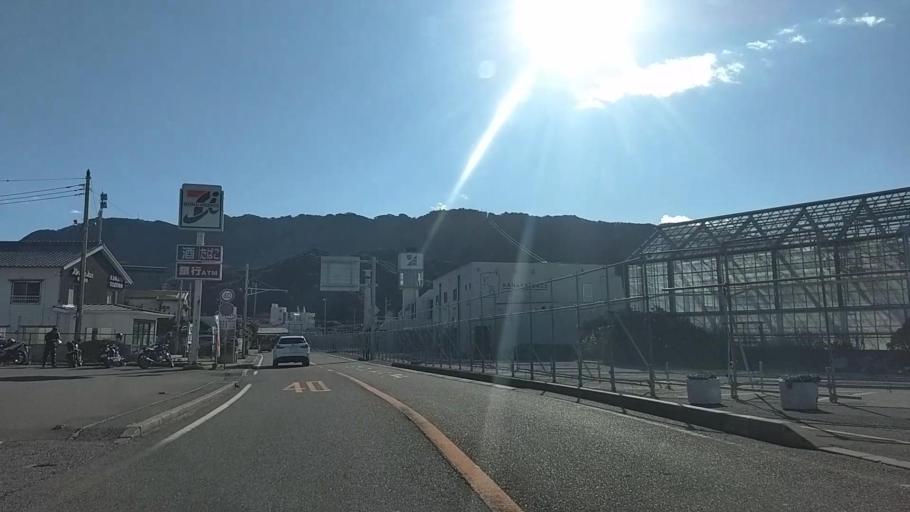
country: JP
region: Chiba
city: Futtsu
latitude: 35.1681
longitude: 139.8199
